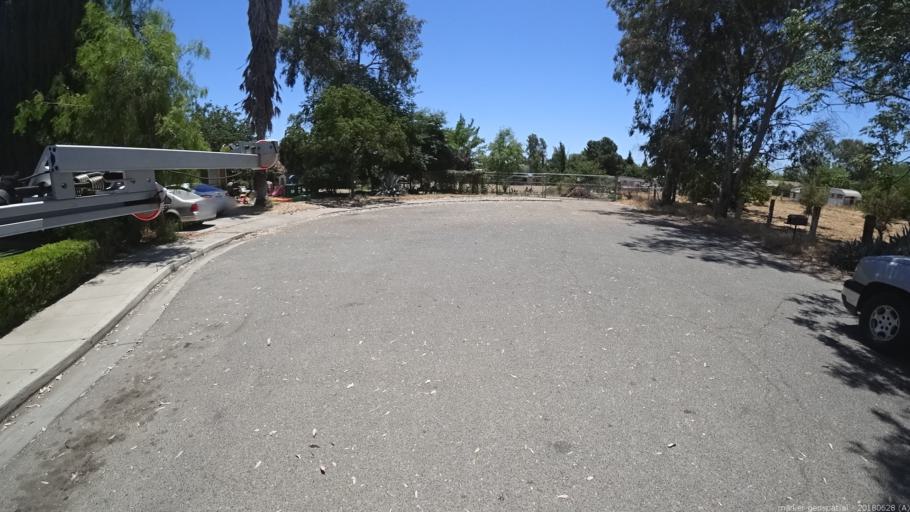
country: US
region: California
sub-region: Madera County
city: Parksdale
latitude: 36.9448
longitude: -120.0238
